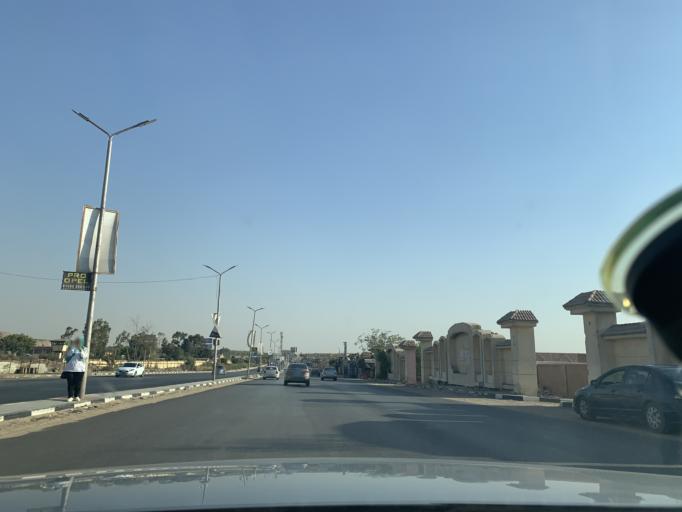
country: EG
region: Muhafazat al Qahirah
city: Cairo
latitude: 30.0309
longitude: 31.3543
